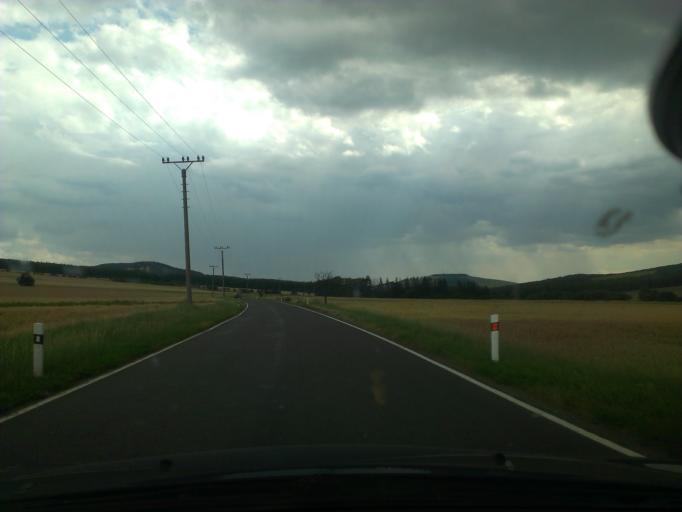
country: CZ
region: South Moravian
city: Velka nad Velickou
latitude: 48.8516
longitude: 17.5222
